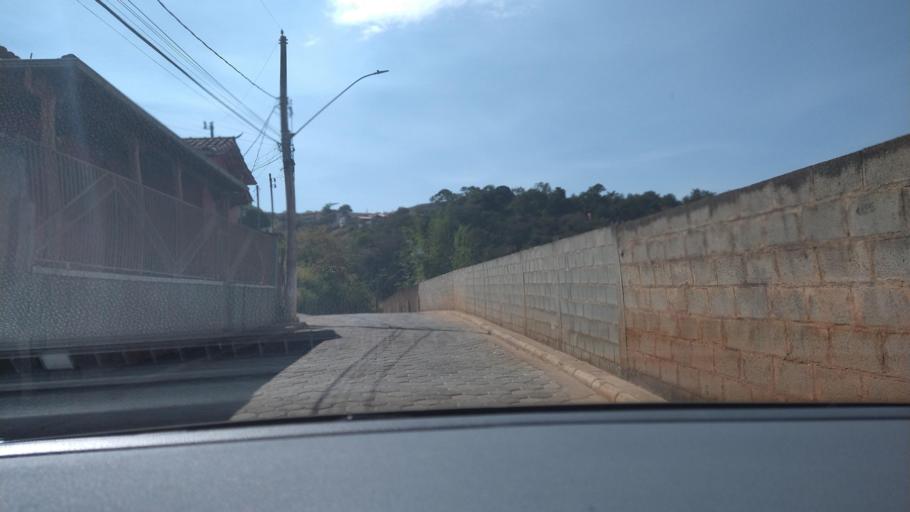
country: BR
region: Minas Gerais
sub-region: Rio Piracicaba
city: Rio Piracicaba
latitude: -19.9295
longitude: -43.1745
